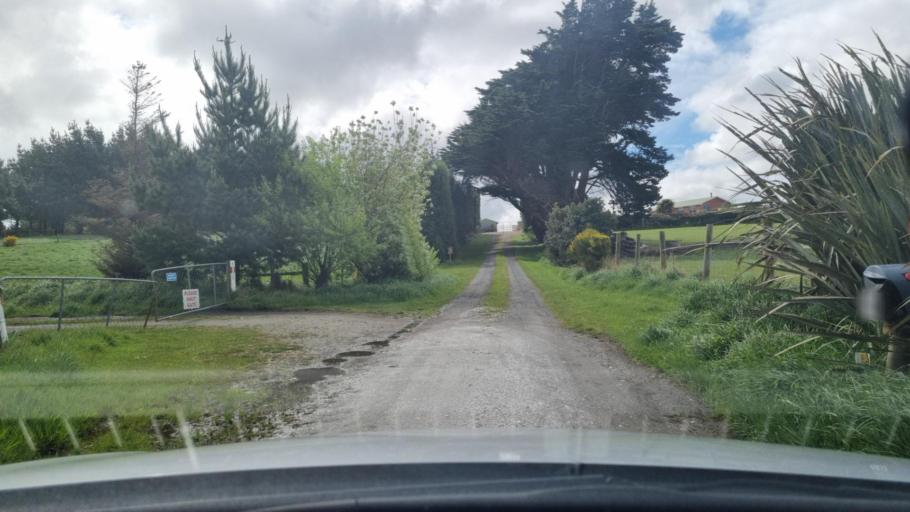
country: NZ
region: Southland
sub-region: Invercargill City
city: Bluff
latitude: -46.5385
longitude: 168.2991
